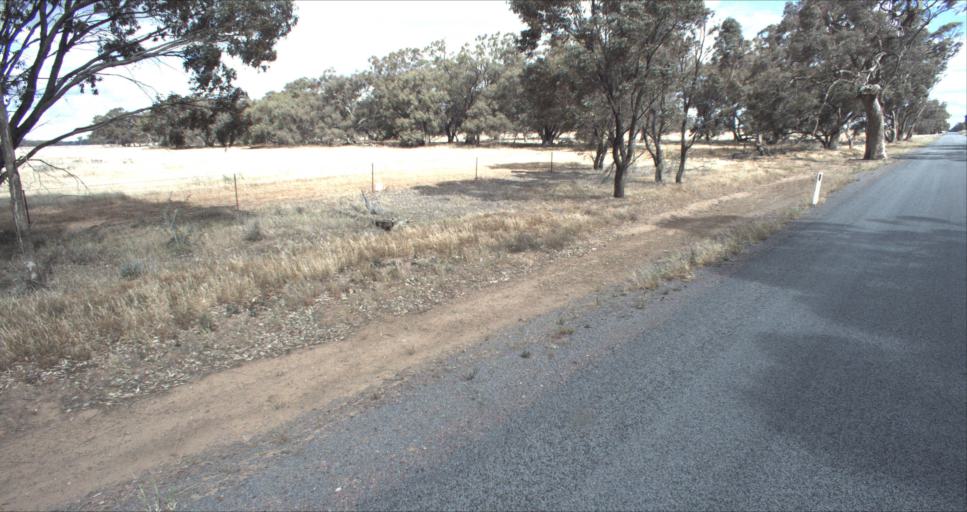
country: AU
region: New South Wales
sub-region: Leeton
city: Leeton
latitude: -34.6671
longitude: 146.3482
